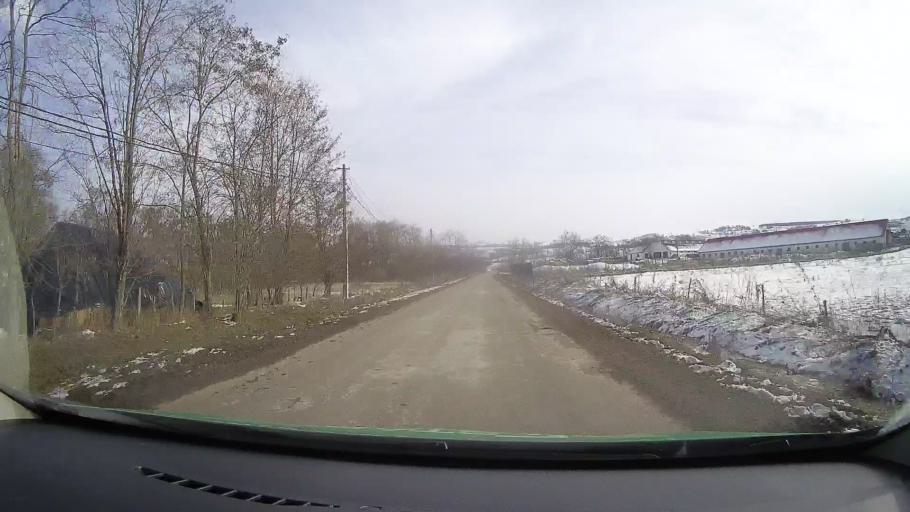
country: RO
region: Mures
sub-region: Comuna Apold
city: Apold
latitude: 46.1206
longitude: 24.8225
